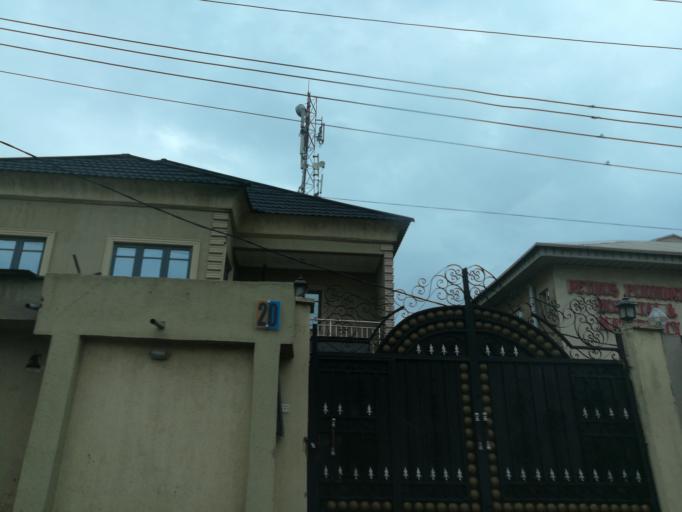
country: NG
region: Lagos
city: Oshodi
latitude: 6.5535
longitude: 3.3426
